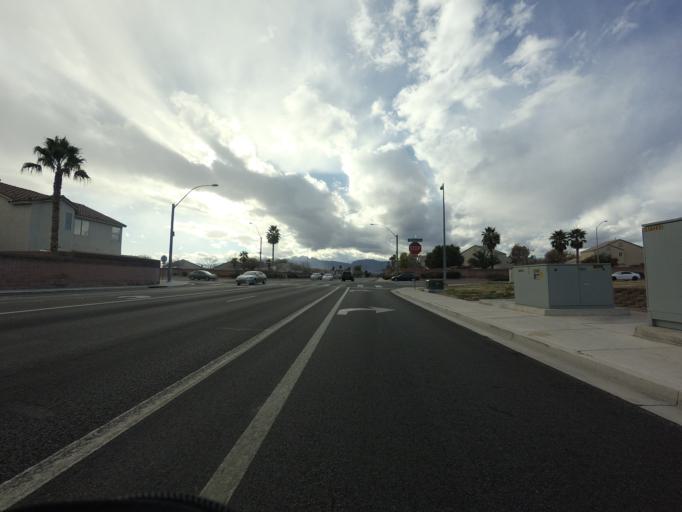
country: US
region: Nevada
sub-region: Clark County
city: North Las Vegas
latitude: 36.2685
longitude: -115.2159
